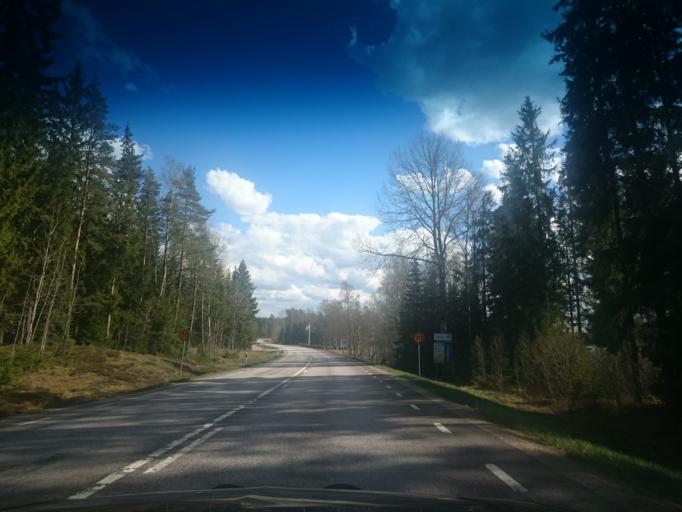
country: SE
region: Kronoberg
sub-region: Vaxjo Kommun
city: Braas
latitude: 57.2381
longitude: 15.1435
